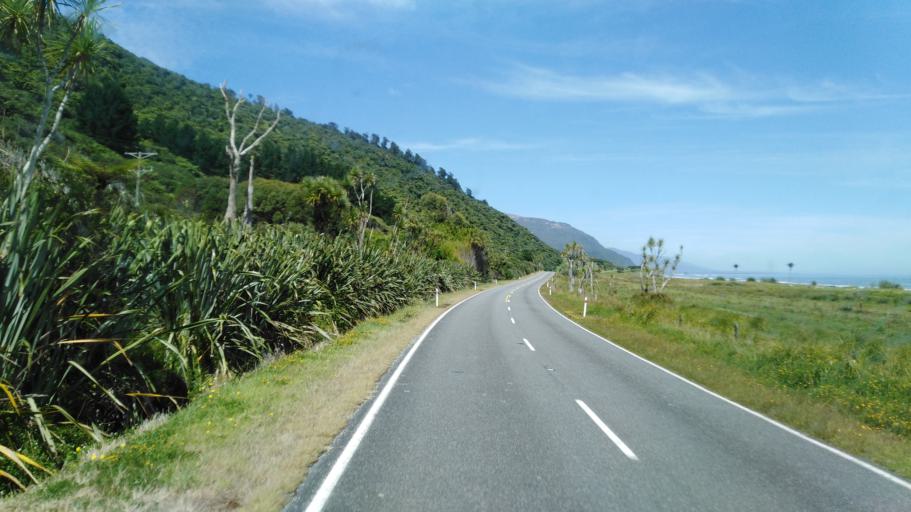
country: NZ
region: West Coast
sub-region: Buller District
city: Westport
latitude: -41.5841
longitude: 171.8962
